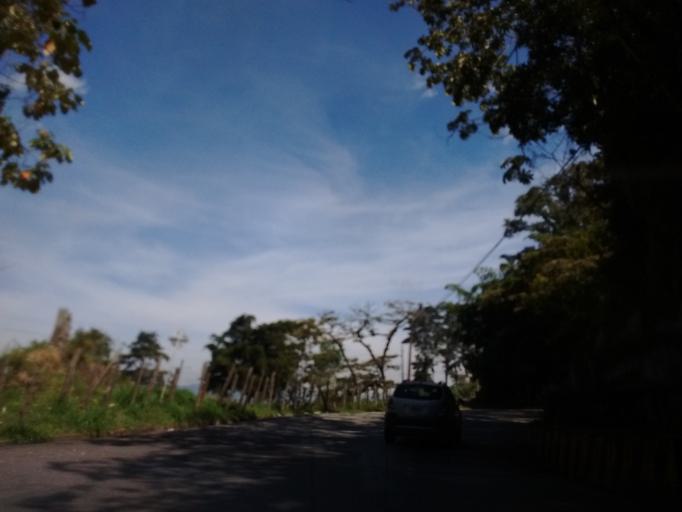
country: CO
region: Antioquia
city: Medellin
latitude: 6.2307
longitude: -75.5157
